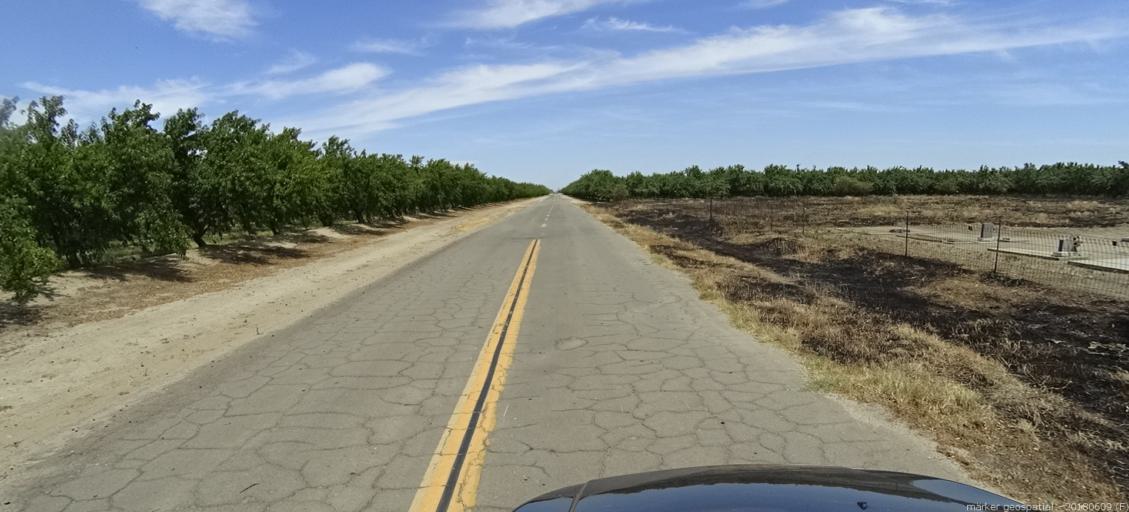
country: US
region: California
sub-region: Madera County
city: Madera
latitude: 36.9093
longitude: -120.1550
